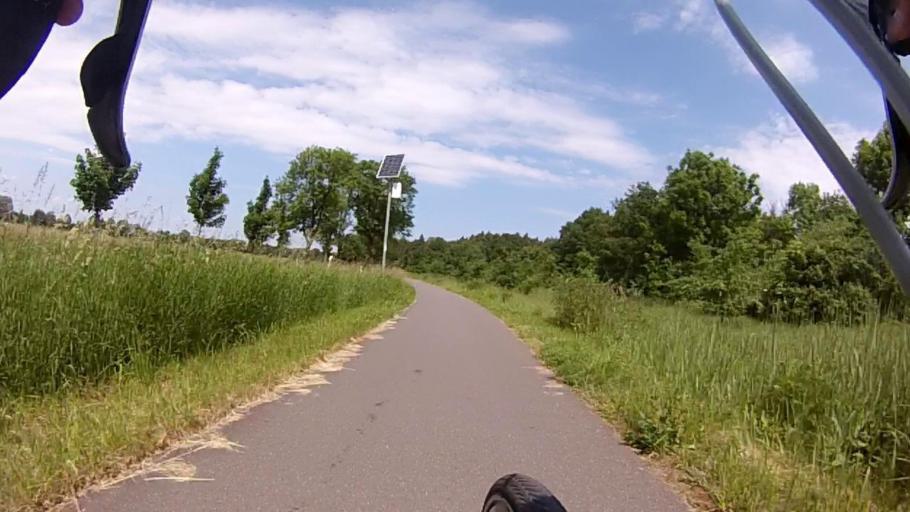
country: DE
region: Brandenburg
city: Liebenwalde
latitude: 52.8535
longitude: 13.4036
